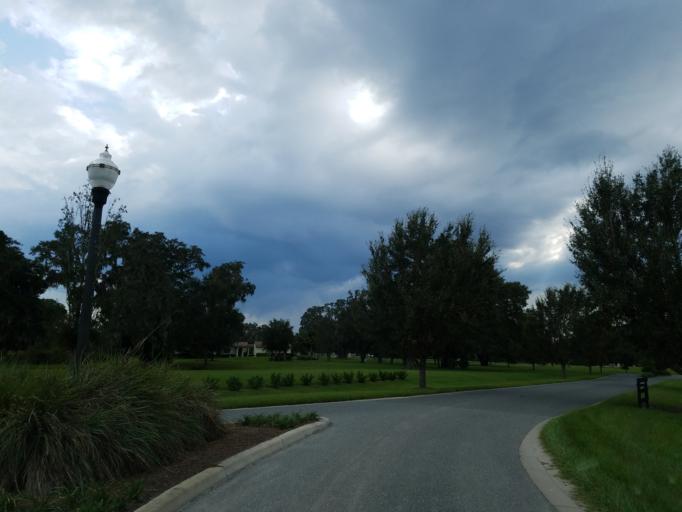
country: US
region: Florida
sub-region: Citrus County
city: Hernando
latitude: 29.0178
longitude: -82.3235
